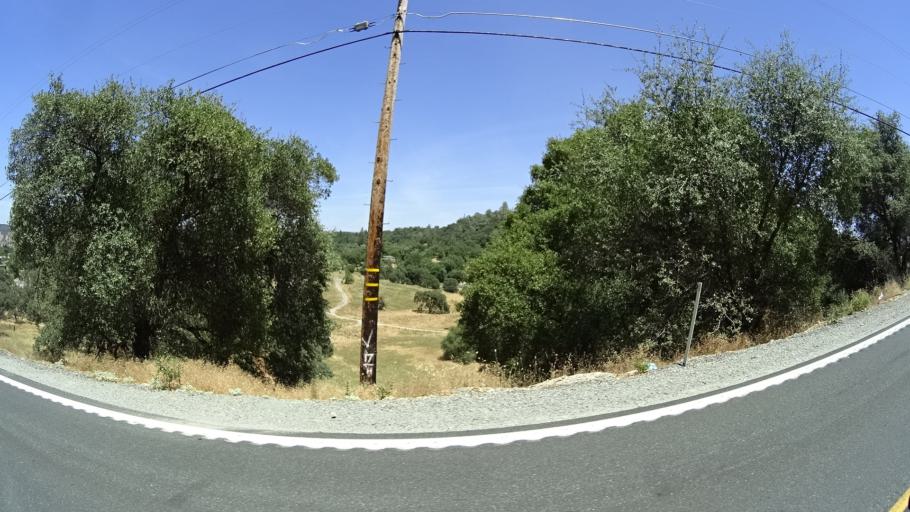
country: US
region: California
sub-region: Amador County
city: Jackson
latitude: 38.2948
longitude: -120.7069
